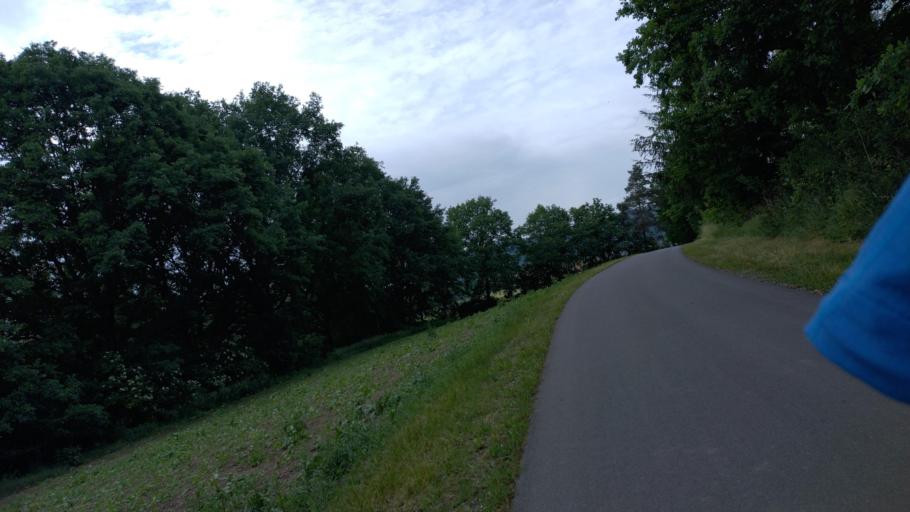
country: DE
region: Bavaria
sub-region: Upper Franconia
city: Harsdorf
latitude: 50.0180
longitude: 11.5770
